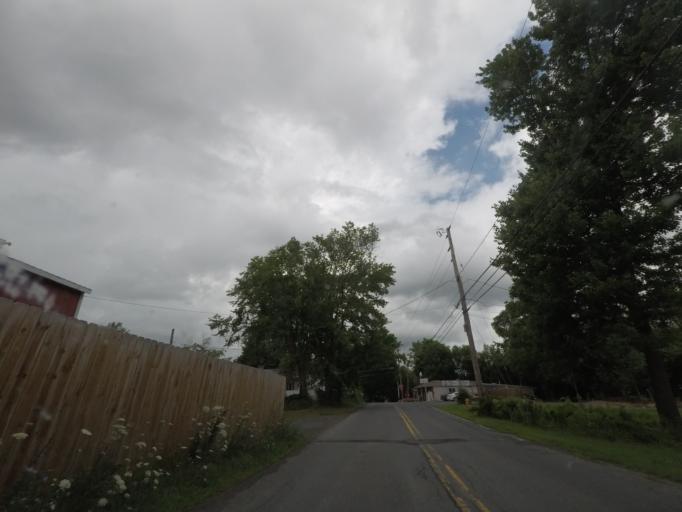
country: US
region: New York
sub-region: Rensselaer County
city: West Sand Lake
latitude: 42.6661
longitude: -73.6274
